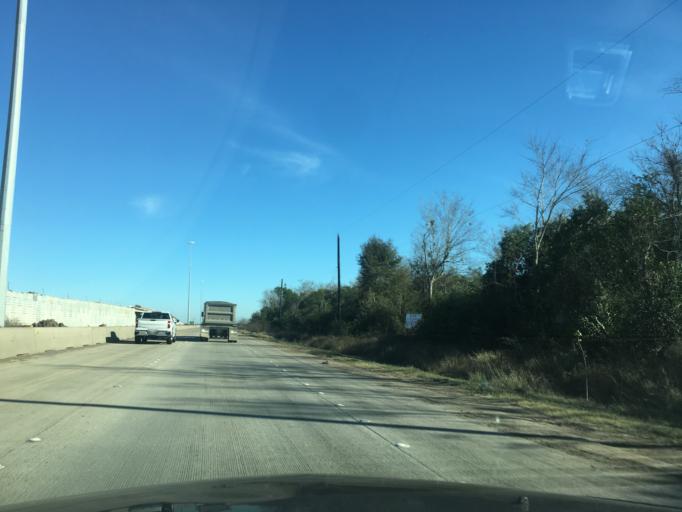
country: US
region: Texas
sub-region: Fort Bend County
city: Rosenberg
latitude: 29.5344
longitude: -95.8485
